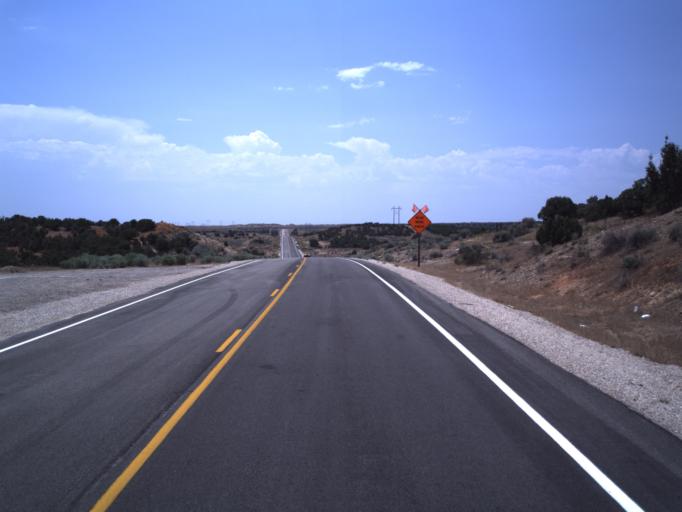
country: US
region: Utah
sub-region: Uintah County
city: Maeser
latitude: 40.4414
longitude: -109.6414
